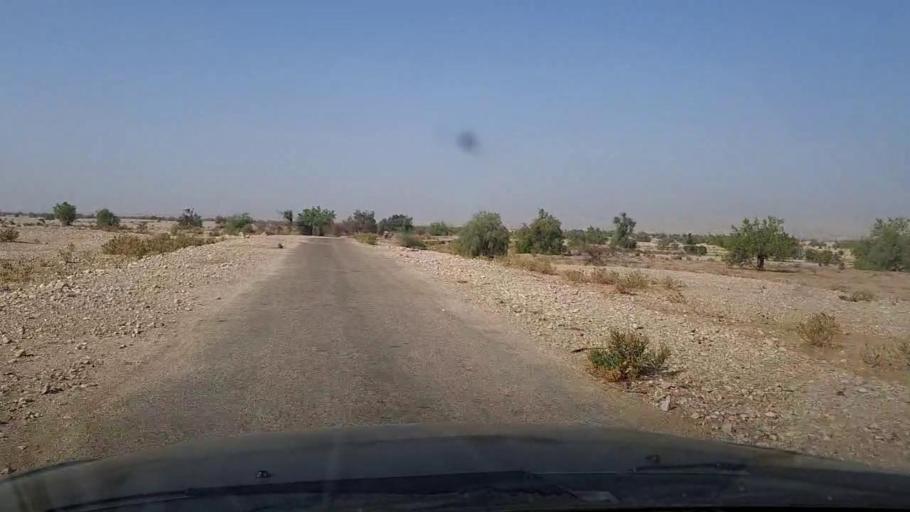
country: PK
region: Sindh
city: Sann
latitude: 25.8887
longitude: 67.9875
